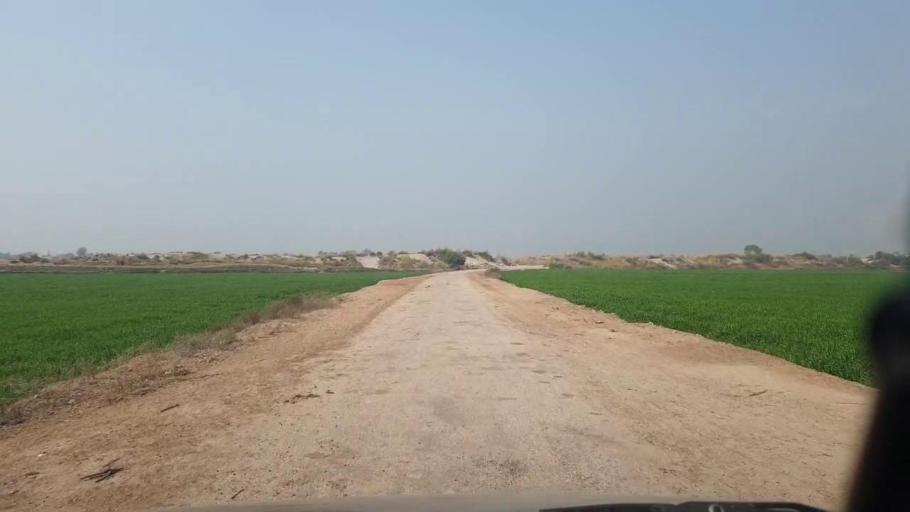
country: PK
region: Sindh
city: Shahdadpur
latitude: 26.0330
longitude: 68.5250
